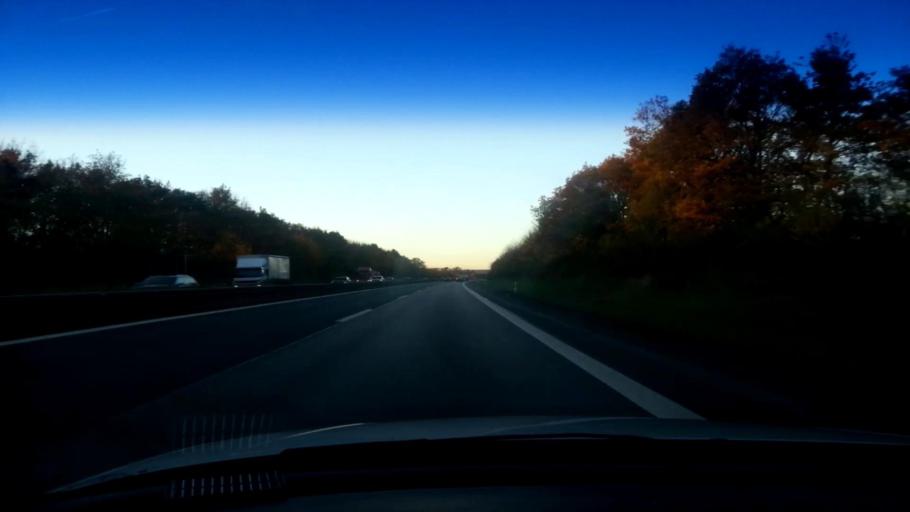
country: DE
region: Bavaria
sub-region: Upper Franconia
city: Altendorf
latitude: 49.8024
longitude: 11.0181
